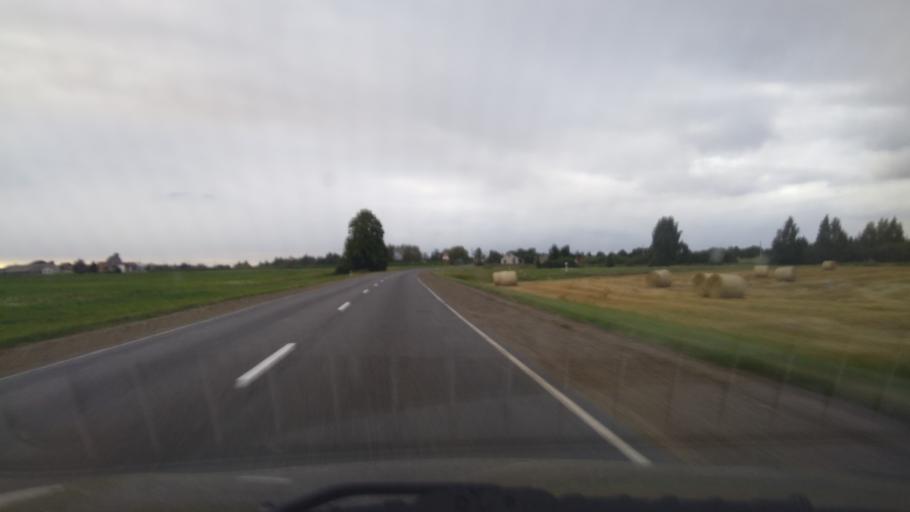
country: BY
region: Brest
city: Byaroza
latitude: 52.4497
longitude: 24.9707
